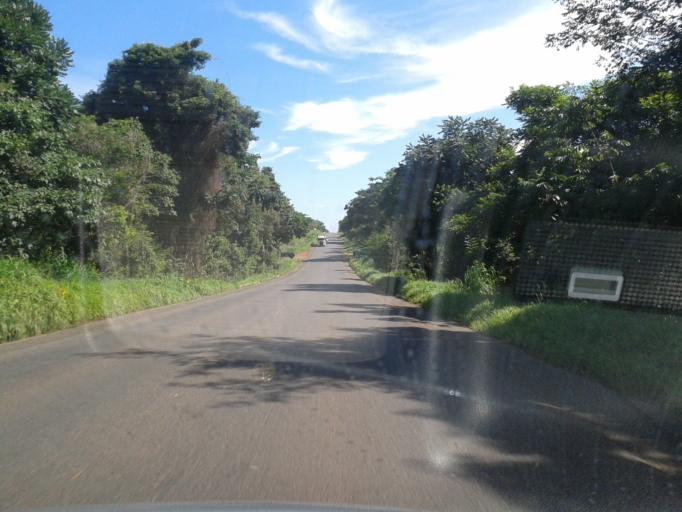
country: BR
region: Goias
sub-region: Piracanjuba
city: Piracanjuba
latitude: -17.2222
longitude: -48.7122
